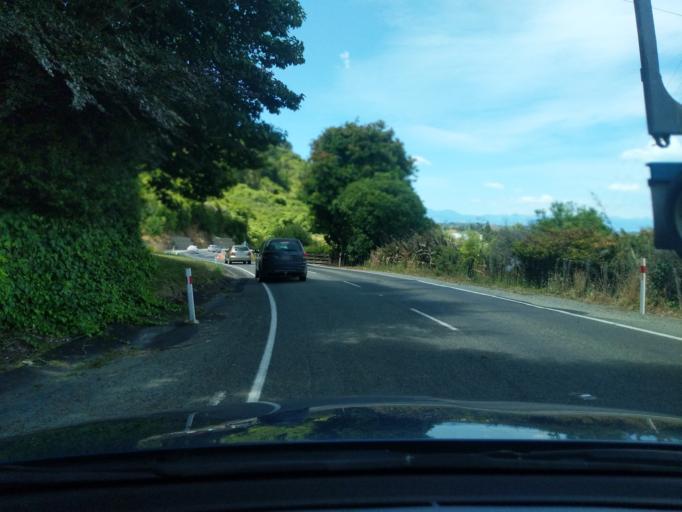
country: NZ
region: Tasman
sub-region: Tasman District
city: Motueka
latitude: -41.0548
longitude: 172.9644
